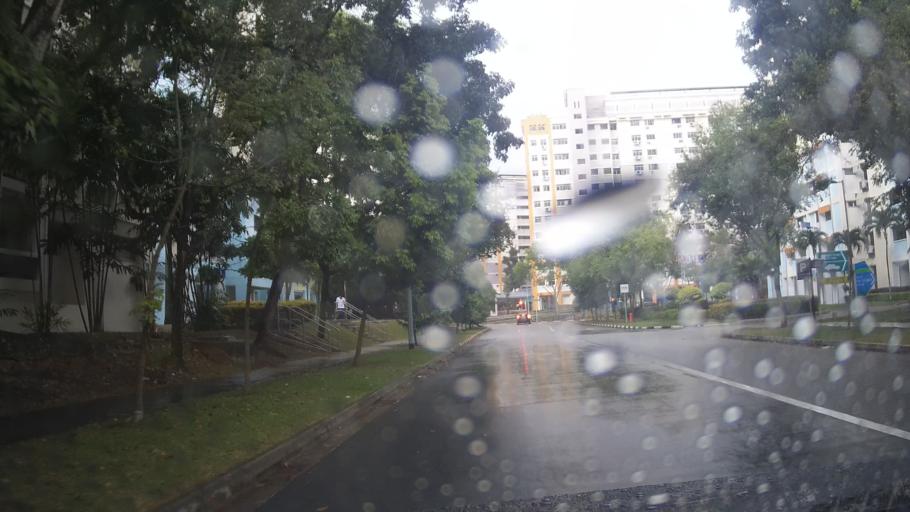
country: MY
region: Johor
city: Johor Bahru
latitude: 1.4413
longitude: 103.7984
